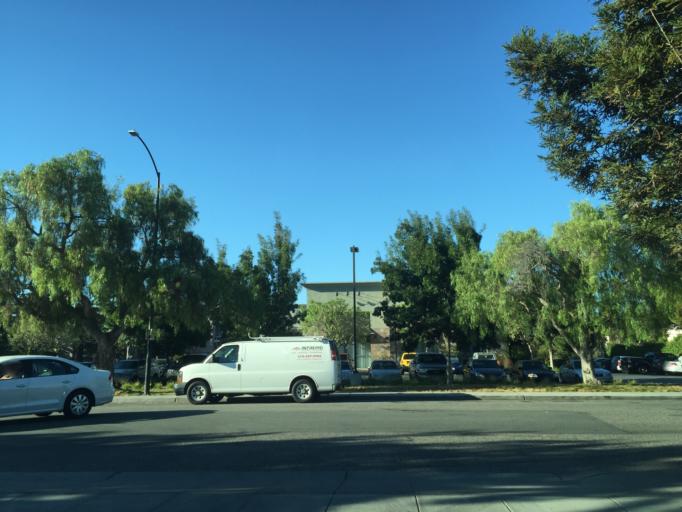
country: US
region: California
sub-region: Santa Clara County
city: Mountain View
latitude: 37.4154
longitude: -122.0769
